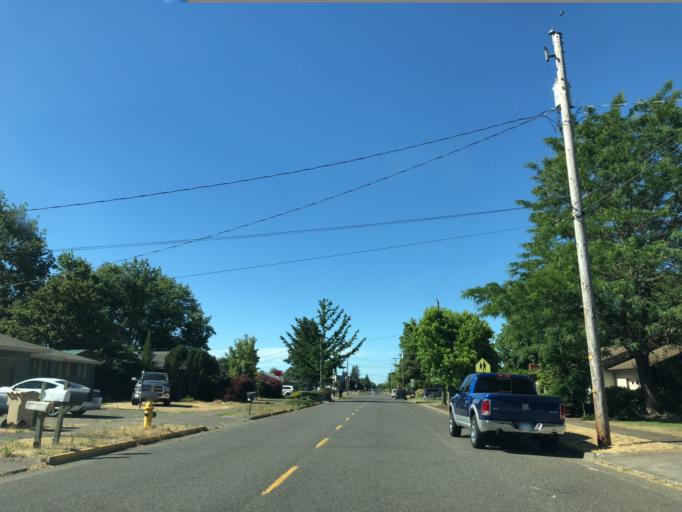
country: US
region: Oregon
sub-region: Linn County
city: Lebanon
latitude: 44.5252
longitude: -122.9127
